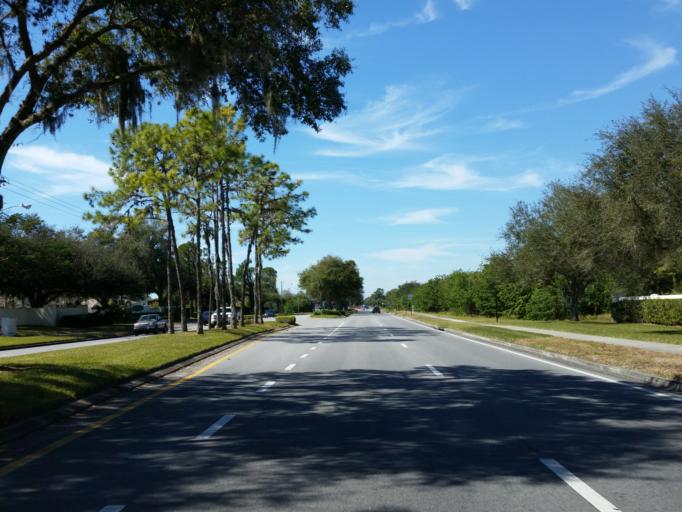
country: US
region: Florida
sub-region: Hillsborough County
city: Balm
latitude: 27.7922
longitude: -82.3123
